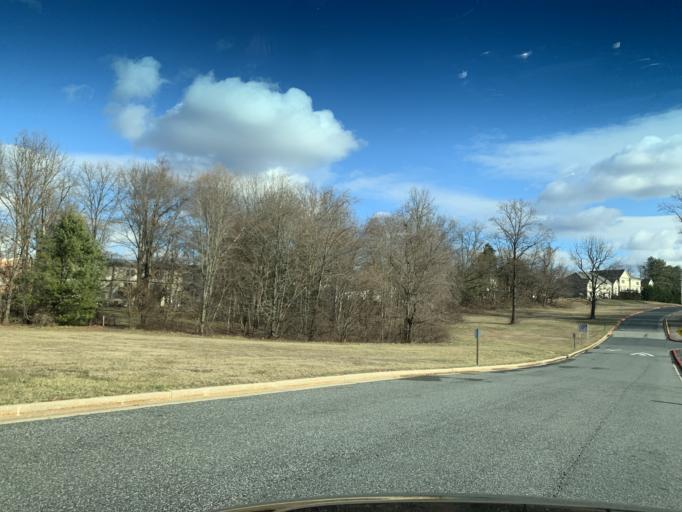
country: US
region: Maryland
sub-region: Harford County
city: South Bel Air
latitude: 39.5278
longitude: -76.3431
